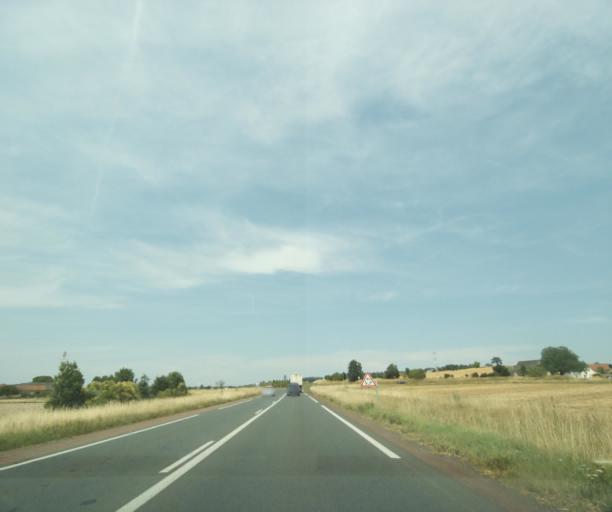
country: FR
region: Poitou-Charentes
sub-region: Departement de la Vienne
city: Chatellerault
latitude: 46.7974
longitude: 0.5606
